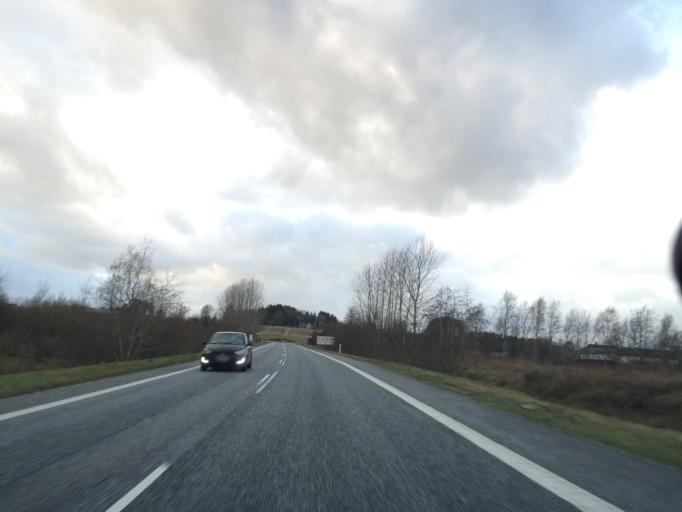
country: DK
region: Central Jutland
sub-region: Silkeborg Kommune
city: Virklund
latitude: 56.1054
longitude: 9.5797
